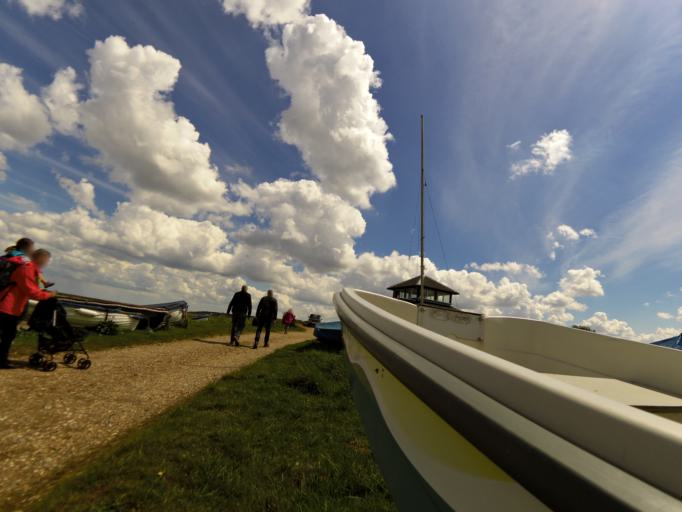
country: GB
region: England
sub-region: Norfolk
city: Briston
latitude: 52.9580
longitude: 0.9854
